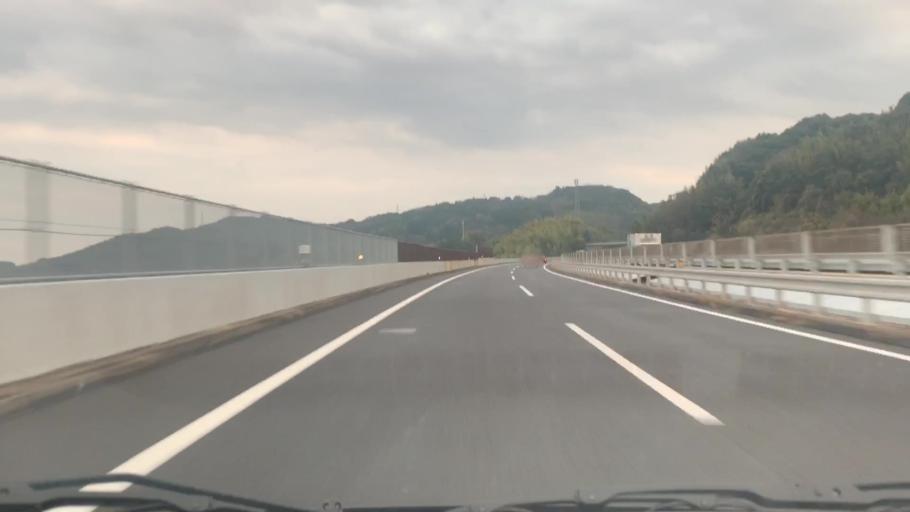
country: JP
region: Nagasaki
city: Omura
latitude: 32.8885
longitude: 129.9920
